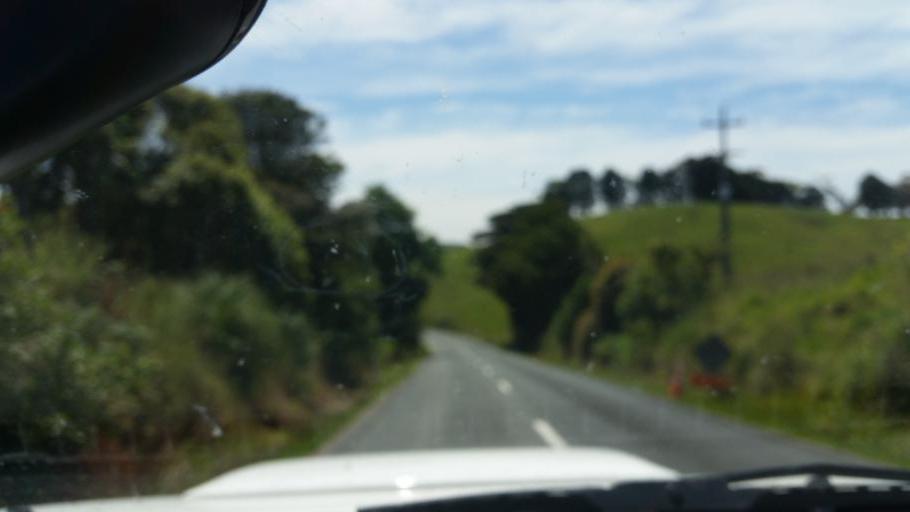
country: NZ
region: Auckland
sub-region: Auckland
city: Wellsford
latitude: -36.1644
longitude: 174.4309
